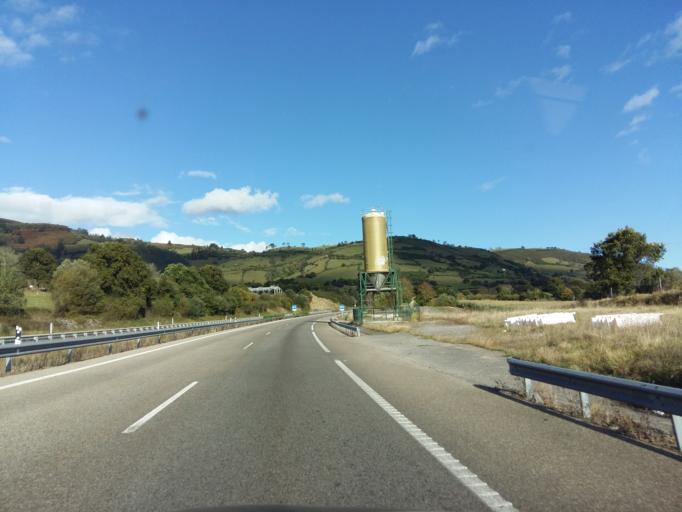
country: ES
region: Asturias
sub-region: Province of Asturias
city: Sariego
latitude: 43.4119
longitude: -5.5653
